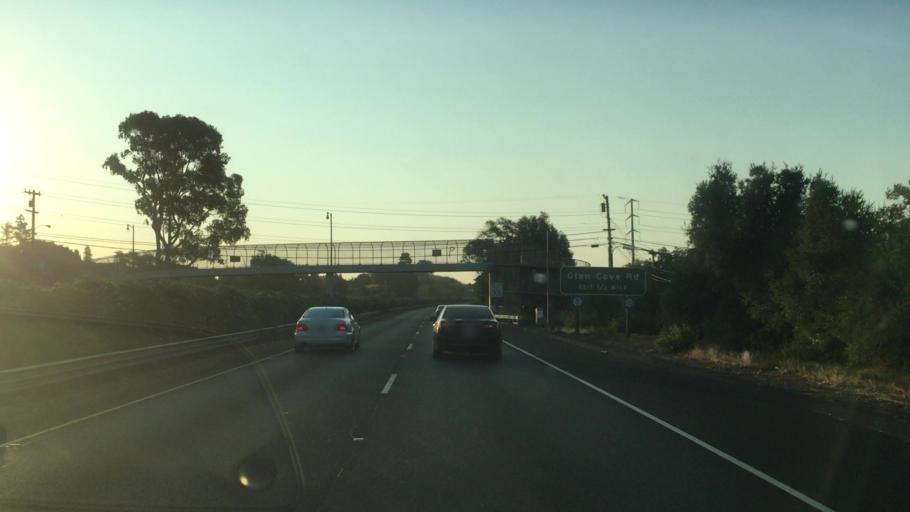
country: US
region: California
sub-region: Solano County
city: Vallejo
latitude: 38.0893
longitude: -122.2223
